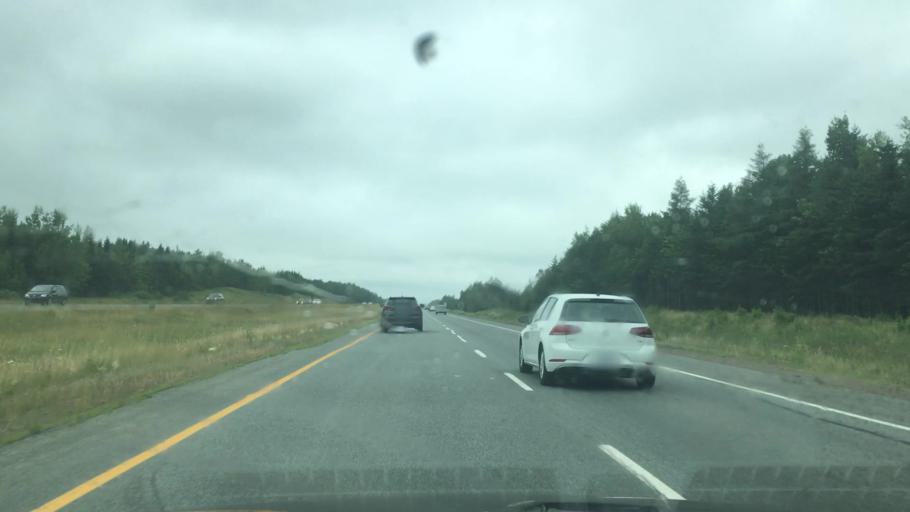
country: CA
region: Nova Scotia
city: Truro
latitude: 45.2717
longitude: -63.2932
